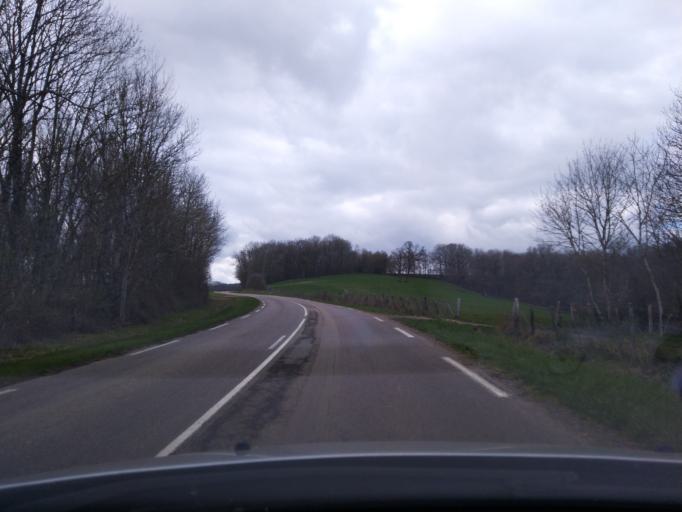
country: FR
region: Bourgogne
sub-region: Departement de l'Yonne
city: Avallon
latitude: 47.5308
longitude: 4.0010
